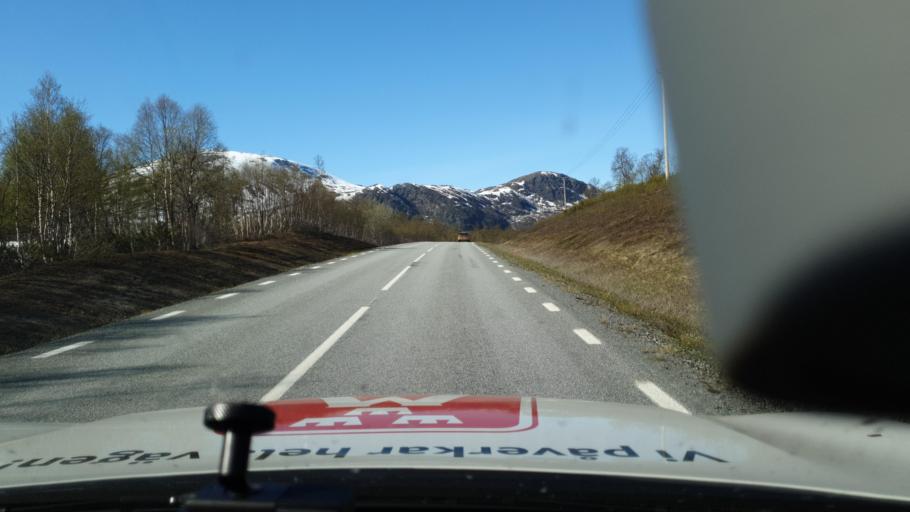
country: NO
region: Nordland
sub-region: Rana
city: Mo i Rana
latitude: 65.9074
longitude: 14.9883
